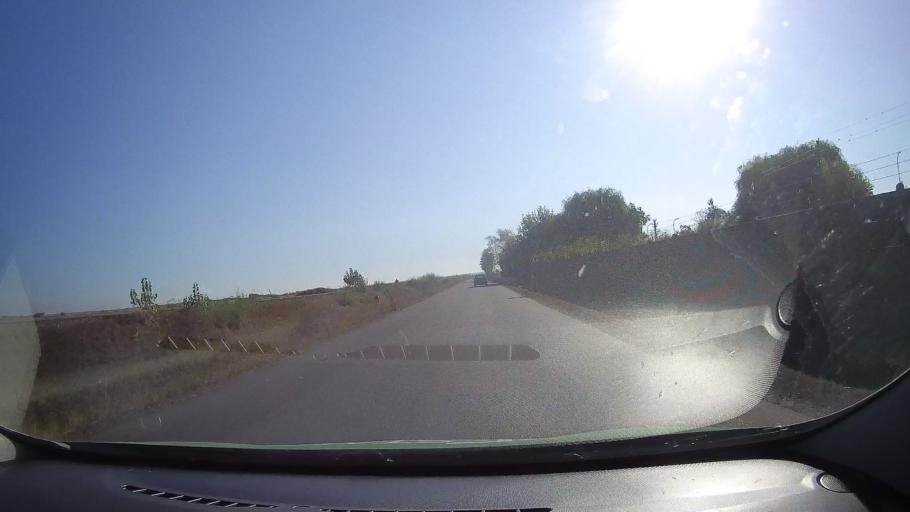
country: RO
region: Satu Mare
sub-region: Comuna Santau
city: Santau
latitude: 47.5069
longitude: 22.5273
